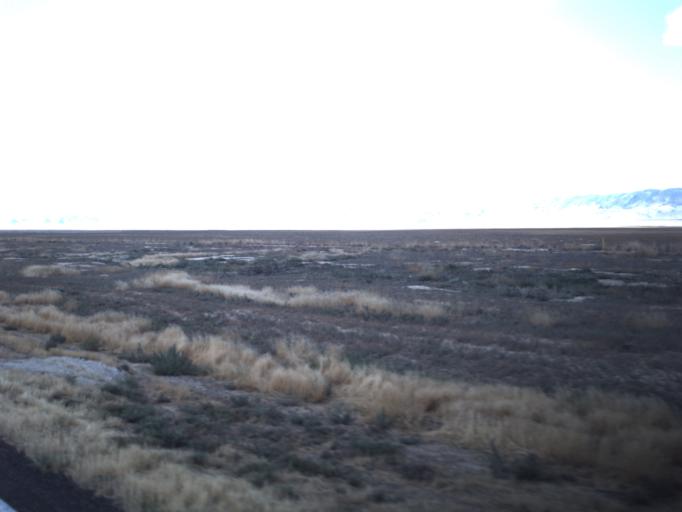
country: US
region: Utah
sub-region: Millard County
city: Delta
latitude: 39.0015
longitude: -112.7870
